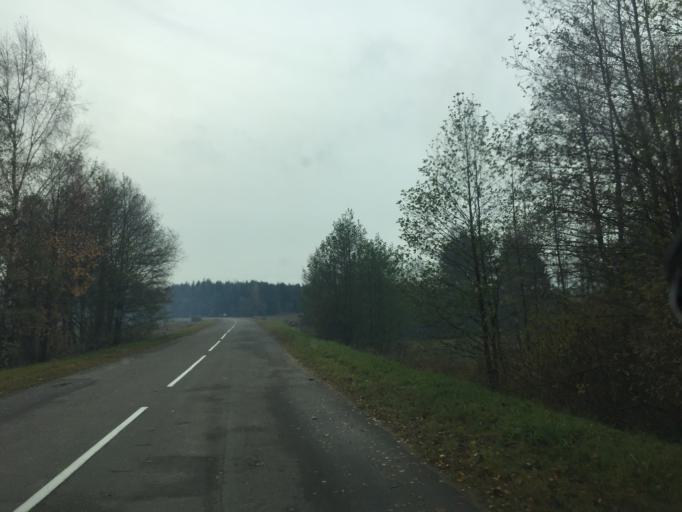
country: BY
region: Mogilev
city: Drybin
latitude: 54.0137
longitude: 31.0214
